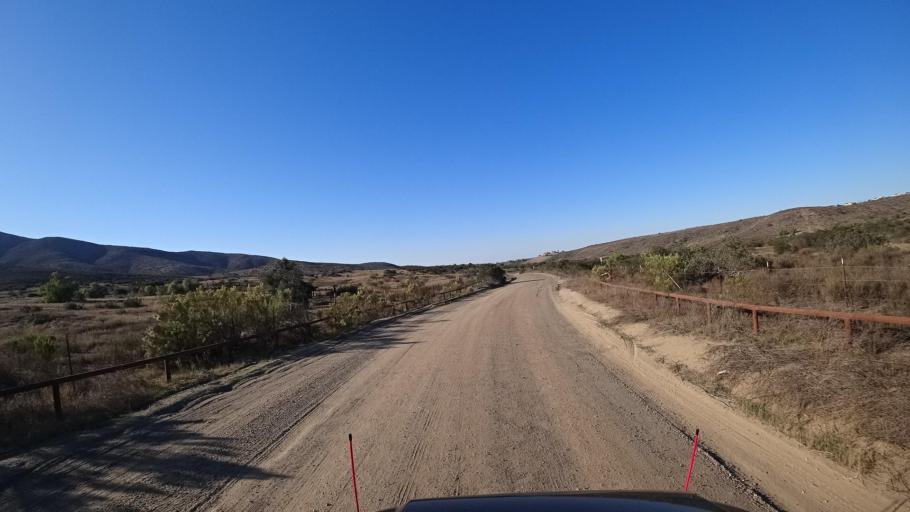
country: US
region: California
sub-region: San Diego County
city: Jamul
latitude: 32.6703
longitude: -116.9234
